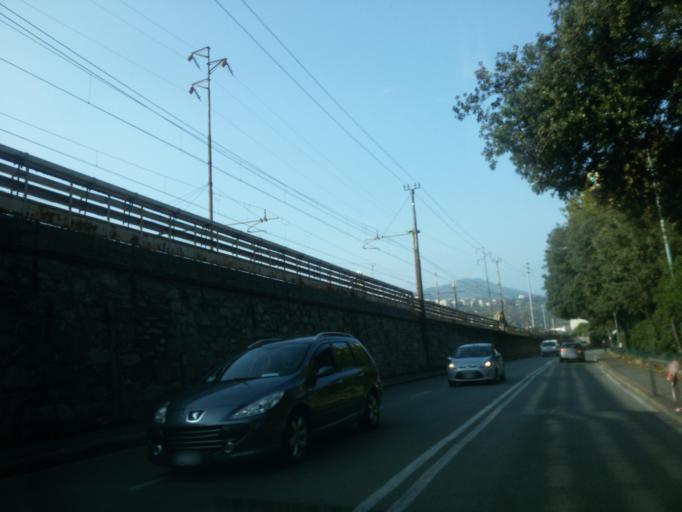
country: IT
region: Liguria
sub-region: Provincia di Genova
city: San Teodoro
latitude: 44.4161
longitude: 8.8856
